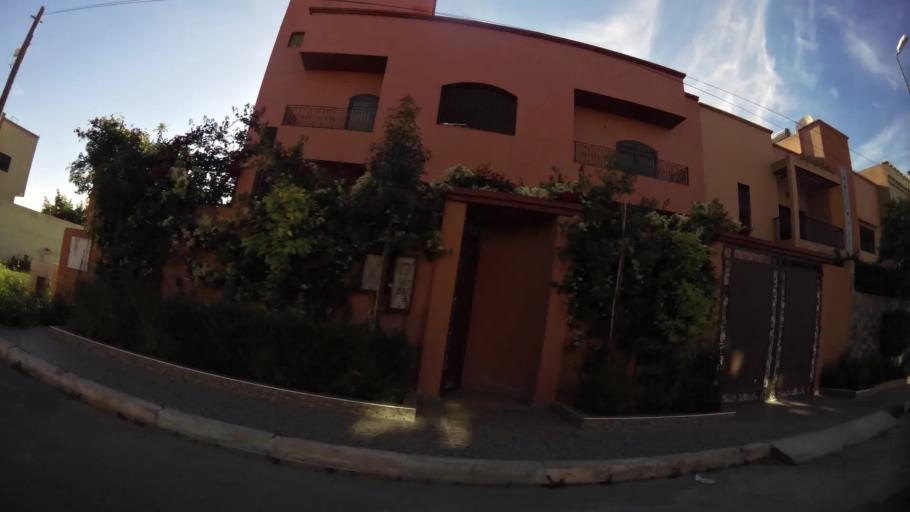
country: MA
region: Marrakech-Tensift-Al Haouz
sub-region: Marrakech
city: Marrakesh
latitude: 31.6810
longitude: -8.0640
